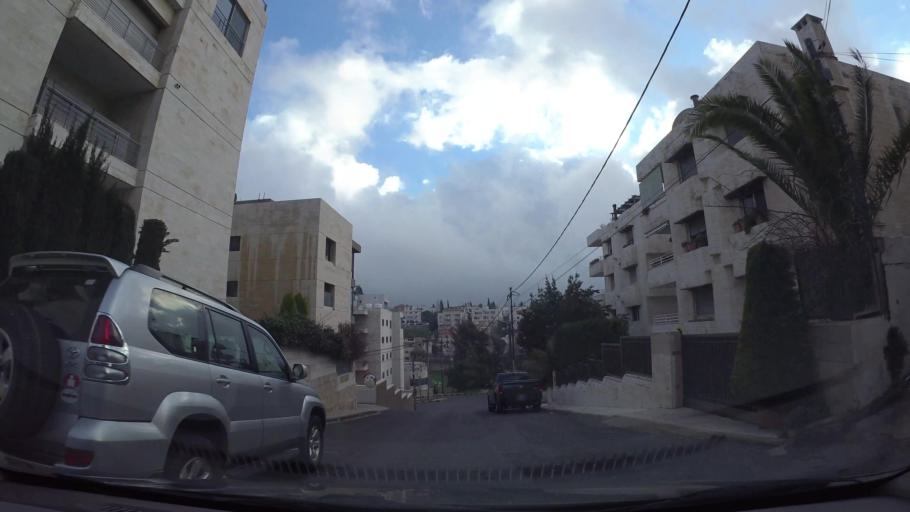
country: JO
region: Amman
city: Amman
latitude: 31.9545
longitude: 35.8903
